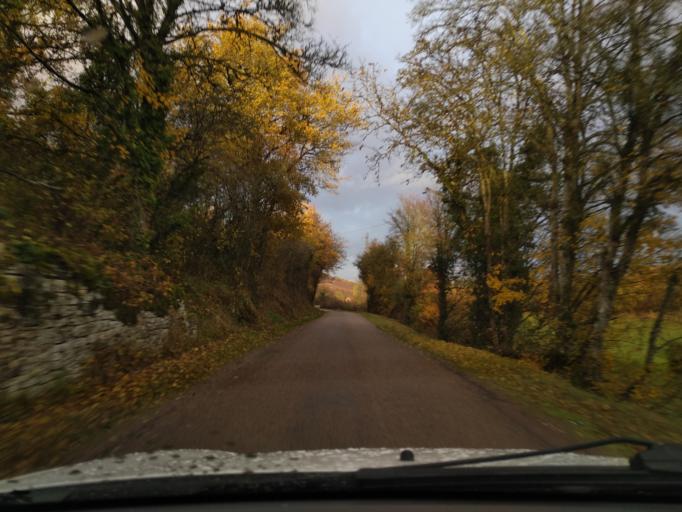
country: FR
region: Bourgogne
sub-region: Departement de Saone-et-Loire
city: Rully
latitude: 46.8858
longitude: 4.7190
